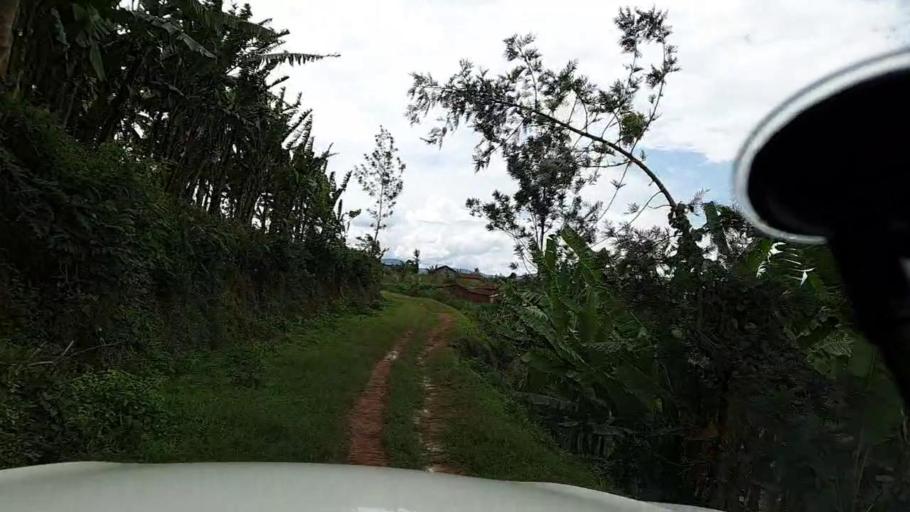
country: RW
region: Southern Province
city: Gitarama
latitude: -2.0738
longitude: 29.6435
